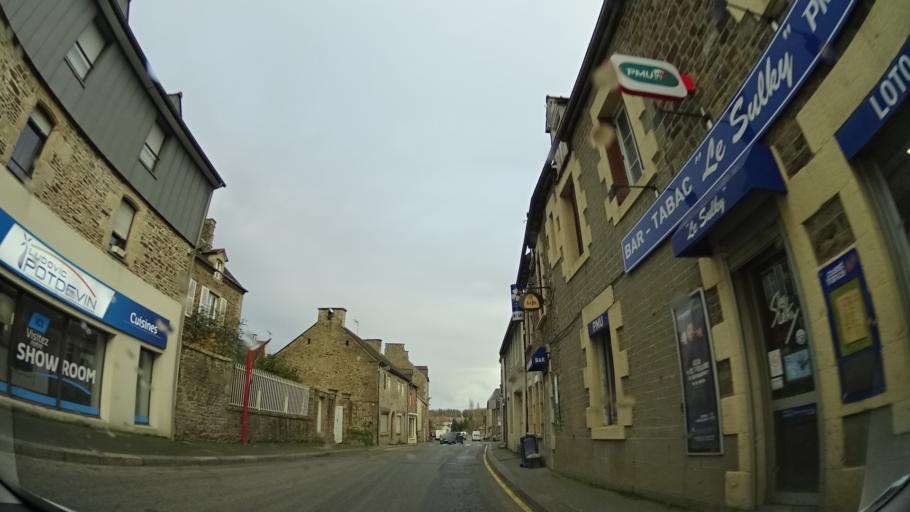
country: FR
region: Brittany
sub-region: Departement des Cotes-d'Armor
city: Evran
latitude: 48.3824
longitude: -1.9806
